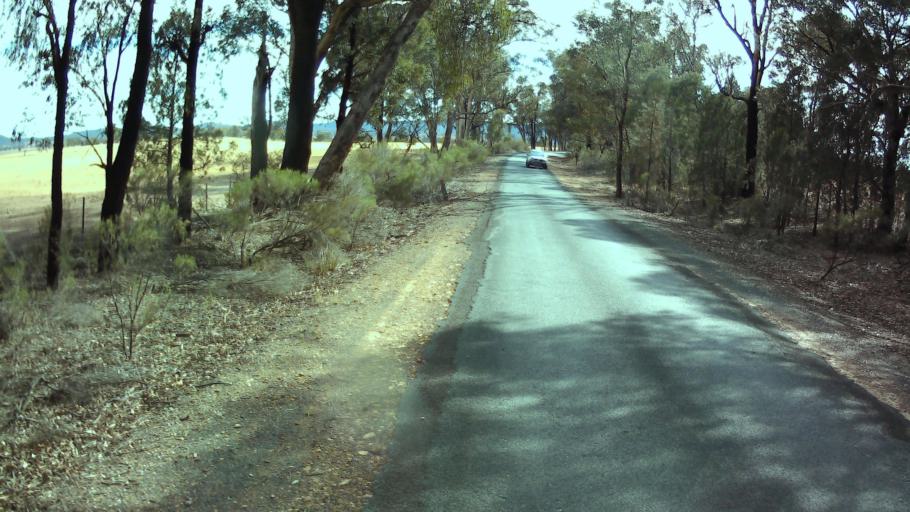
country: AU
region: New South Wales
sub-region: Weddin
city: Grenfell
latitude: -33.8516
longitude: 148.2208
